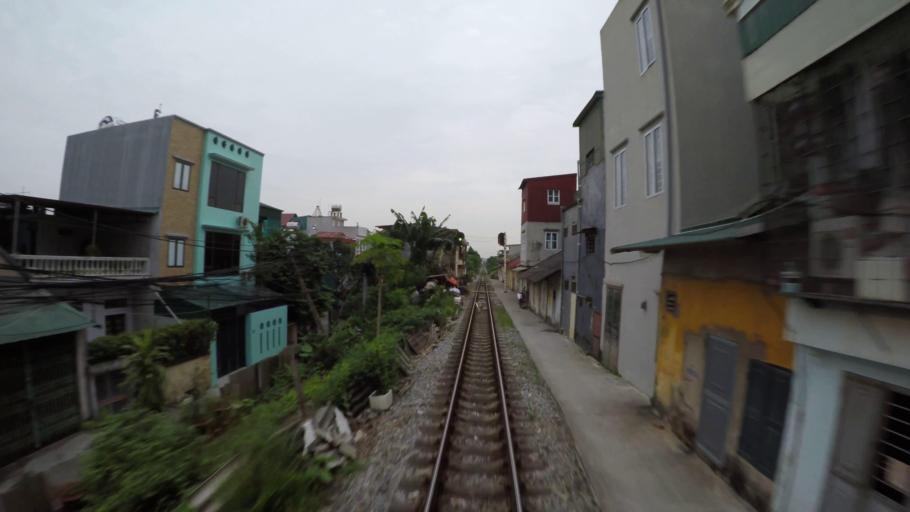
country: VN
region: Ha Noi
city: Hoan Kiem
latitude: 21.0478
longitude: 105.8930
